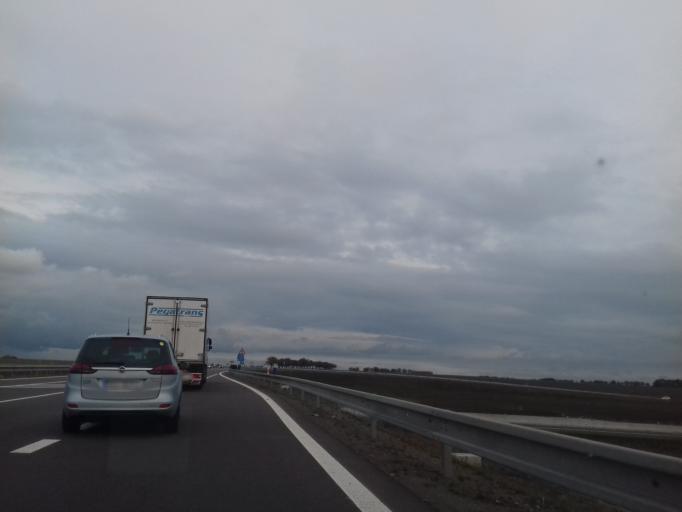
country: CZ
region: Pardubicky
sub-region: Okres Chrudim
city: Slatinany
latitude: 49.9457
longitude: 15.8212
